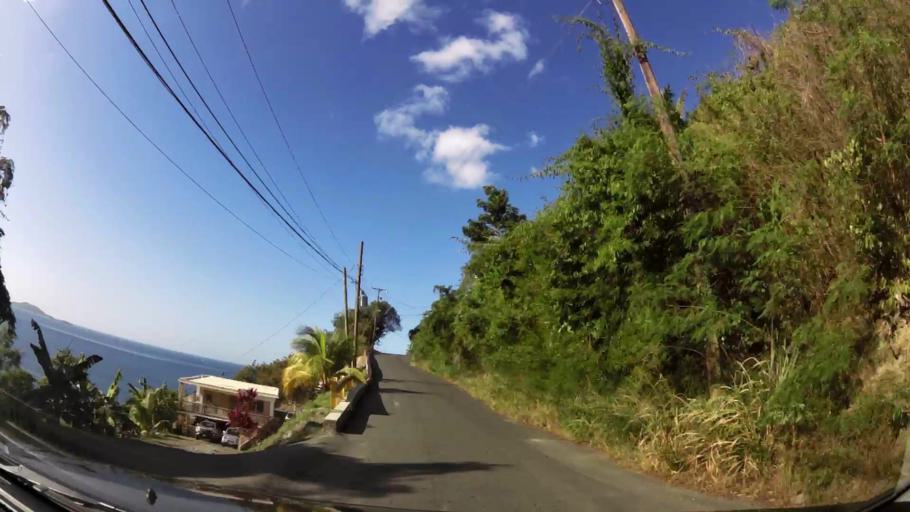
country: VG
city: Road Town
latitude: 18.4192
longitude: -64.6633
